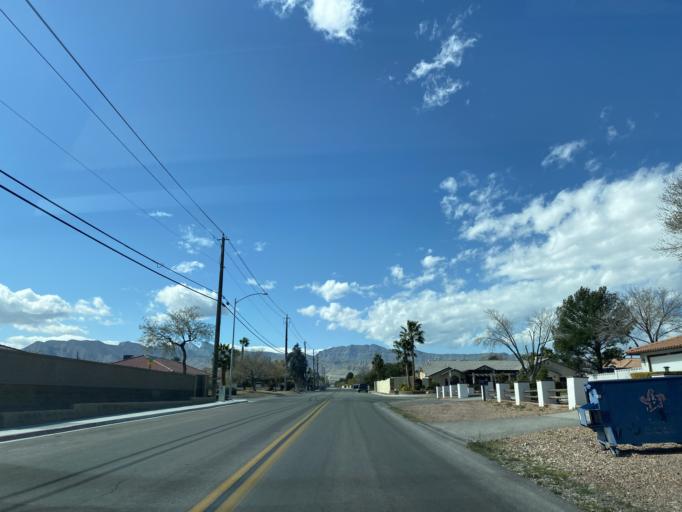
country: US
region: Nevada
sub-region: Clark County
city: Summerlin South
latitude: 36.2556
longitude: -115.2758
